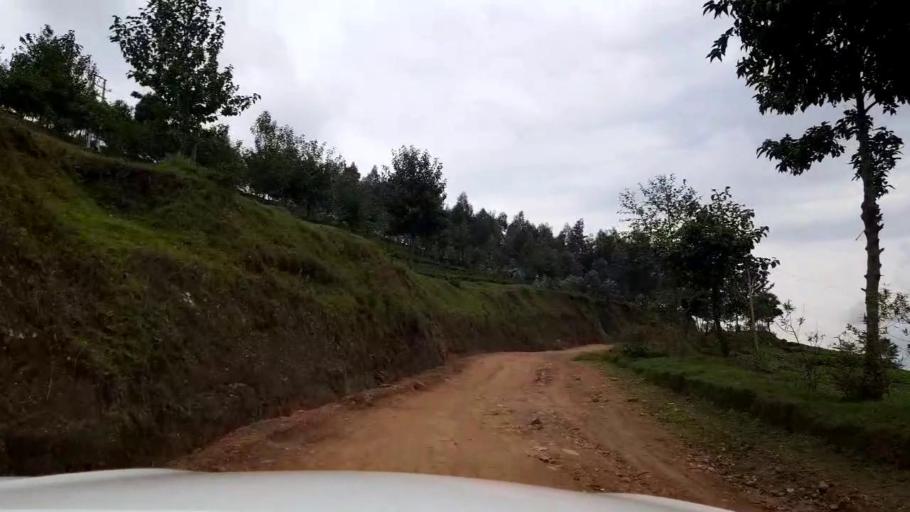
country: RW
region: Western Province
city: Kibuye
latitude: -1.9582
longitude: 29.4020
